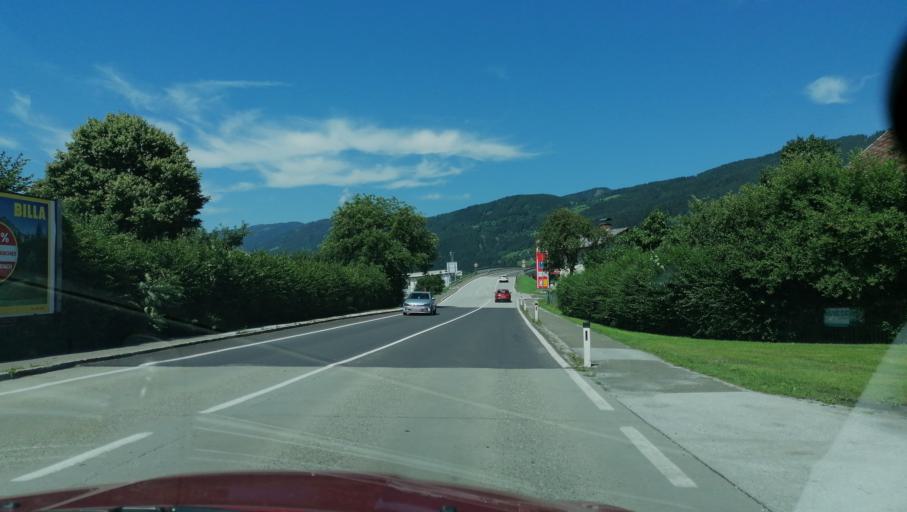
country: AT
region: Styria
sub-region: Politischer Bezirk Liezen
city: Trieben
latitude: 47.4890
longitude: 14.4850
